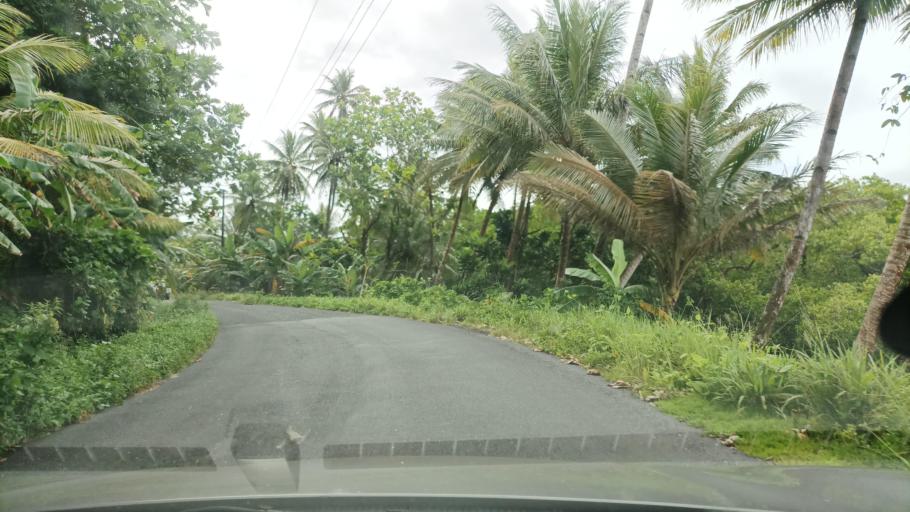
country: FM
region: Pohnpei
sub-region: Kolonia Municipality
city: Kolonia
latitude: 6.9606
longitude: 158.2776
